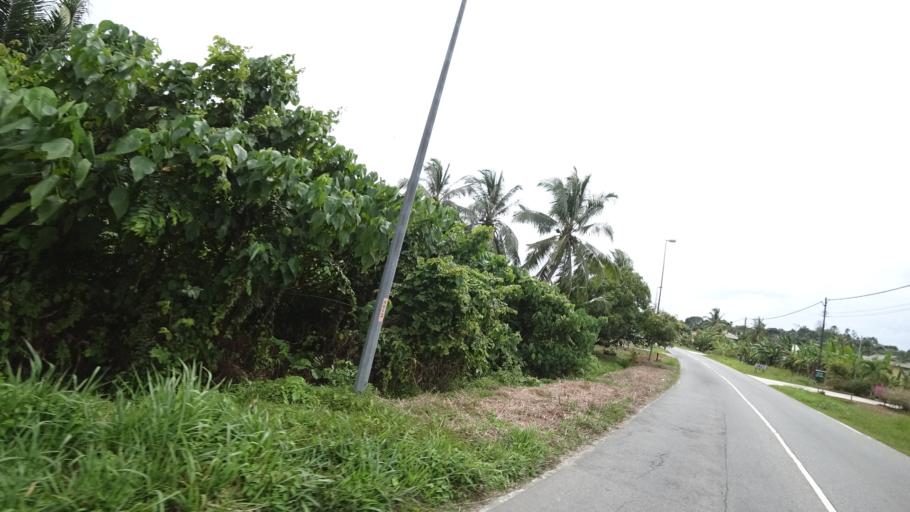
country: BN
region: Tutong
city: Tutong
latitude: 4.8173
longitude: 114.7068
